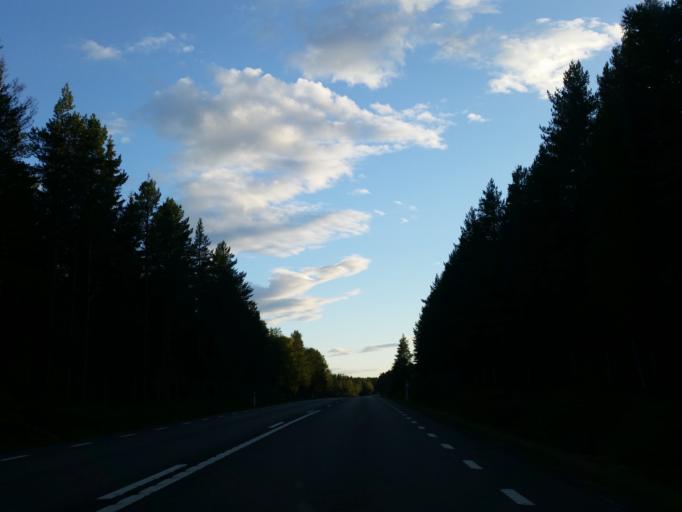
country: SE
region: Vaesterbotten
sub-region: Robertsfors Kommun
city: Robertsfors
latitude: 64.0060
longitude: 20.8030
